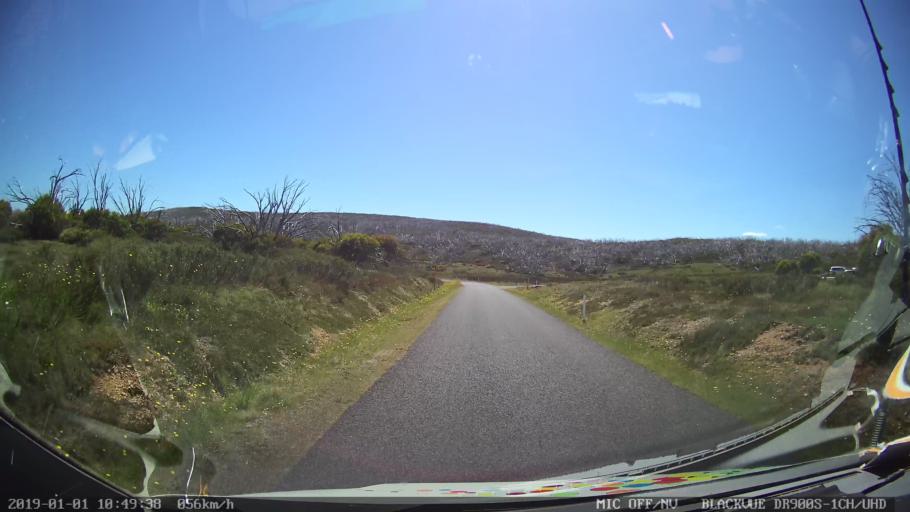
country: AU
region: New South Wales
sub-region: Snowy River
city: Jindabyne
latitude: -36.0341
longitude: 148.3724
